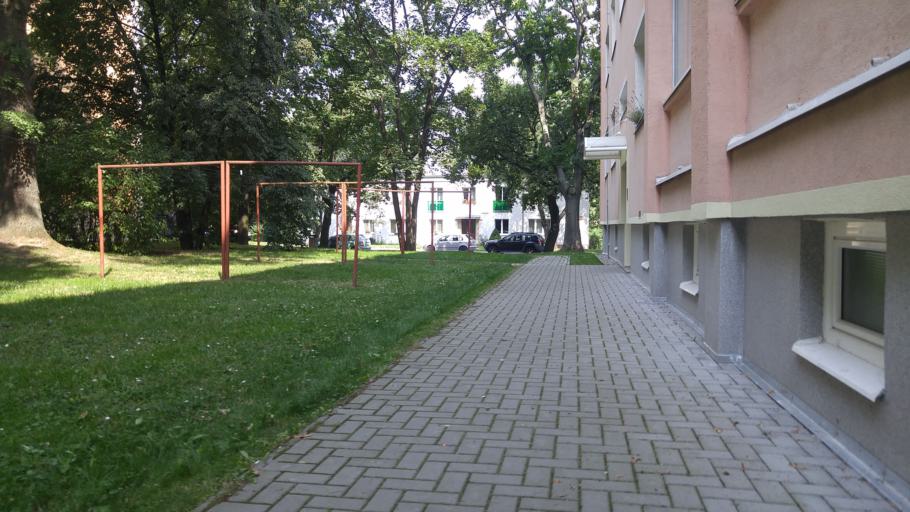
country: CZ
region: Central Bohemia
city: Horomerice
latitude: 50.0905
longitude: 14.3474
